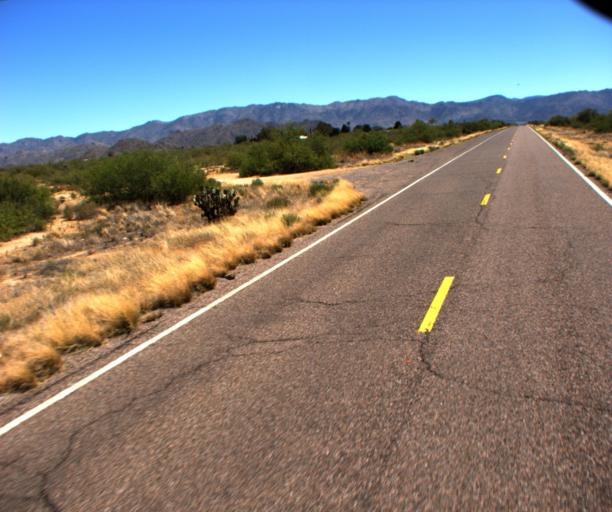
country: US
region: Arizona
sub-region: Yavapai County
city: Congress
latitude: 34.1514
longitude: -112.8801
